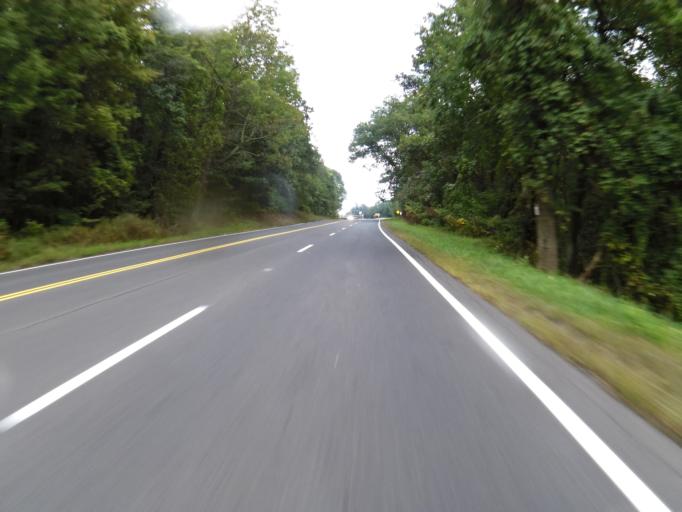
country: US
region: Virginia
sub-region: Page County
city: Luray
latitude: 38.6614
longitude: -78.3255
